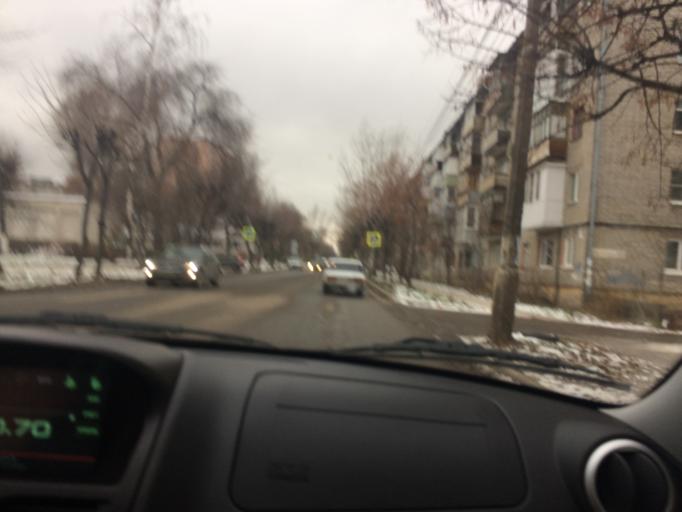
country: RU
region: Rjazan
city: Ryazan'
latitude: 54.6213
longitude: 39.7222
